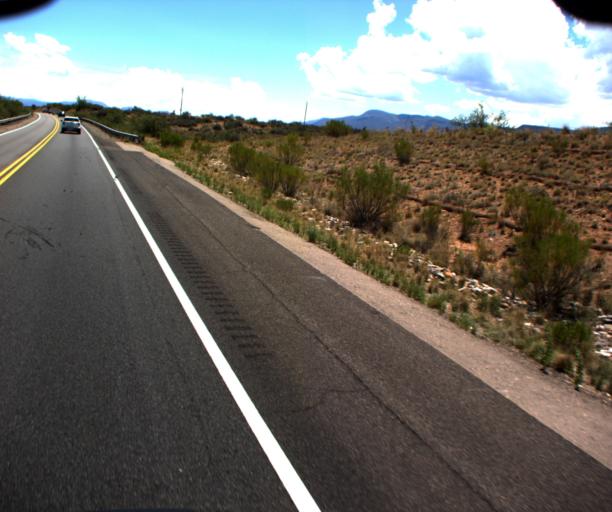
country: US
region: Arizona
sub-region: Yavapai County
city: Cornville
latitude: 34.6257
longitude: -111.9303
